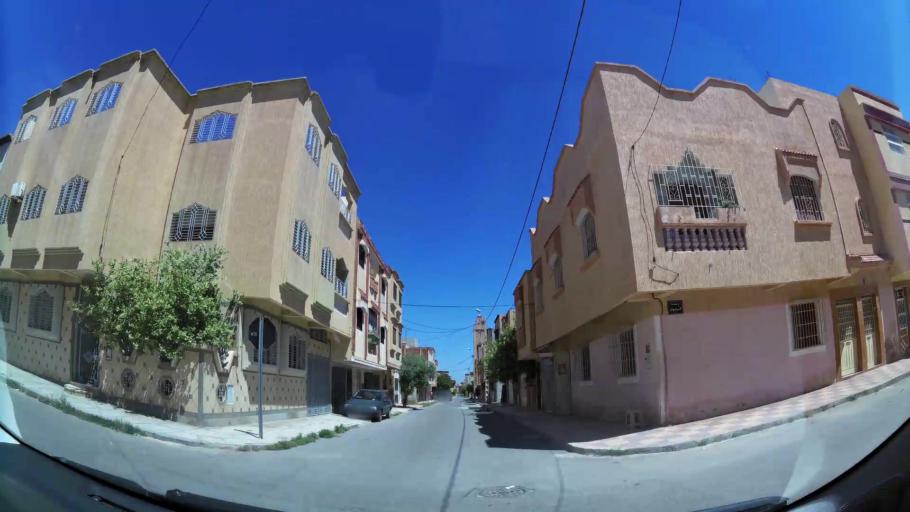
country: MA
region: Oriental
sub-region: Oujda-Angad
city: Oujda
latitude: 34.6673
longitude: -1.8837
